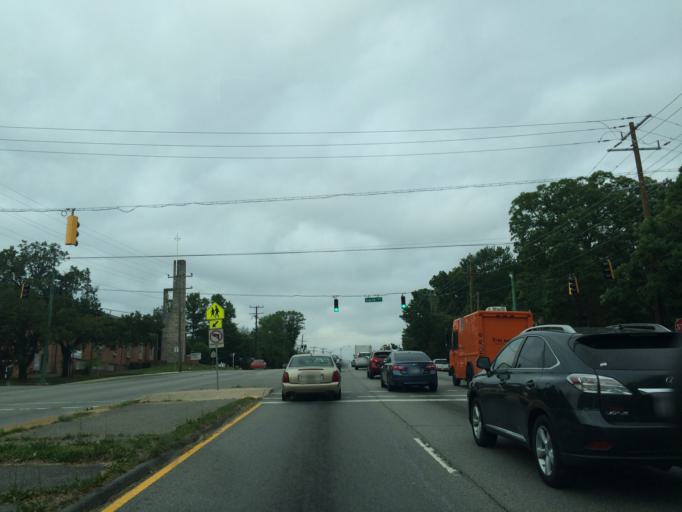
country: US
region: Maryland
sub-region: Prince George's County
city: Chillum
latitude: 38.9781
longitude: -76.9916
